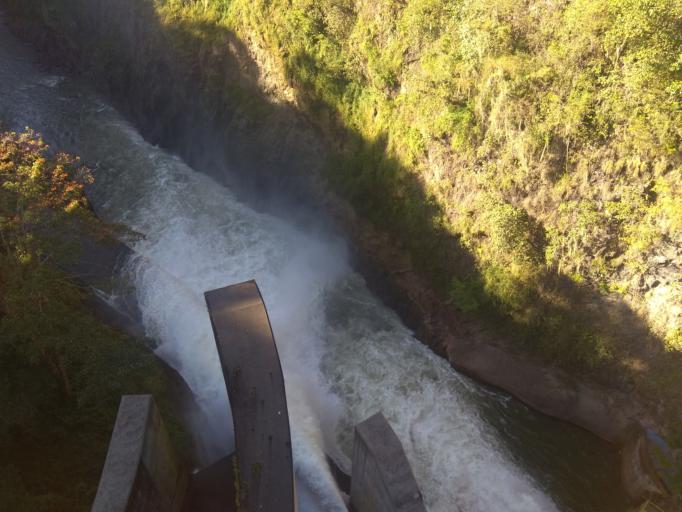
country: CR
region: Cartago
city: Paraiso
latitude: 9.8406
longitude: -83.8044
